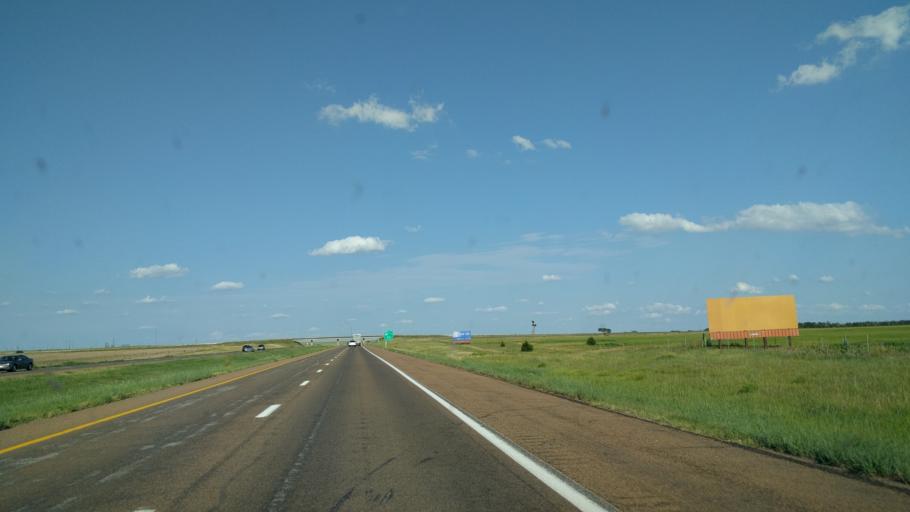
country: US
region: Kansas
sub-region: Ellis County
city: Hays
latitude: 38.9216
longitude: -99.3981
